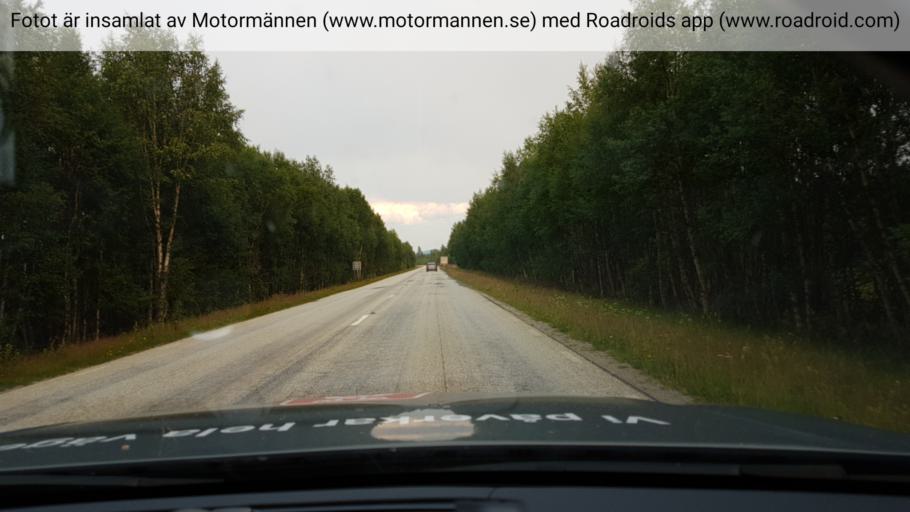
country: SE
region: Jaemtland
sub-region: Harjedalens Kommun
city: Sveg
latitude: 62.4124
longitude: 13.5726
